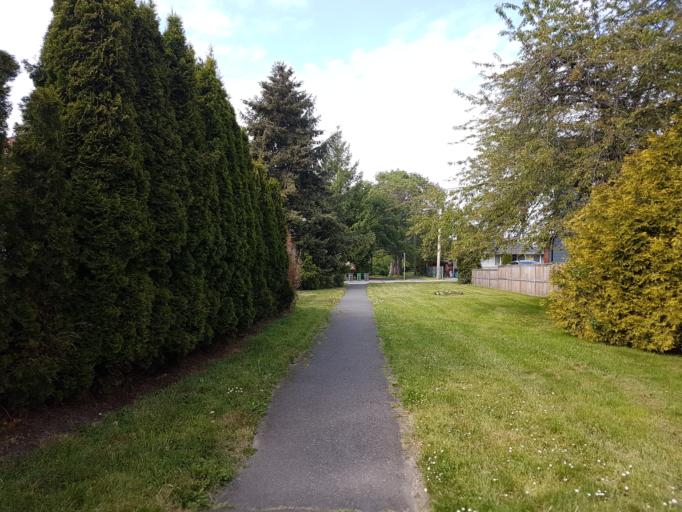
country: CA
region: British Columbia
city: Oak Bay
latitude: 48.4862
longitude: -123.3345
